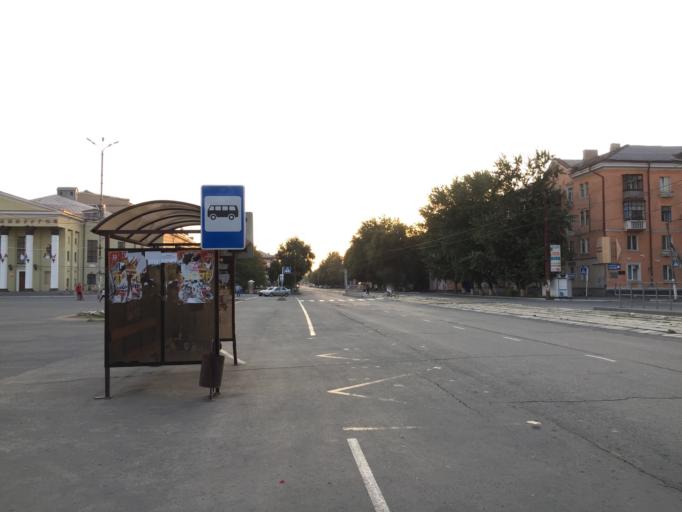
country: RU
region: Orenburg
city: Novotroitsk
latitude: 51.1956
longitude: 58.3252
